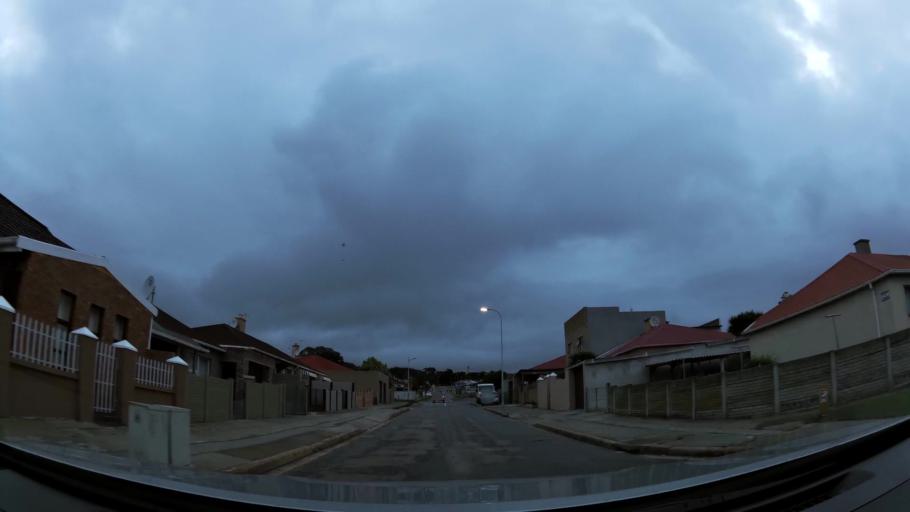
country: ZA
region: Eastern Cape
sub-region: Nelson Mandela Bay Metropolitan Municipality
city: Port Elizabeth
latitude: -33.9407
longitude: 25.5951
